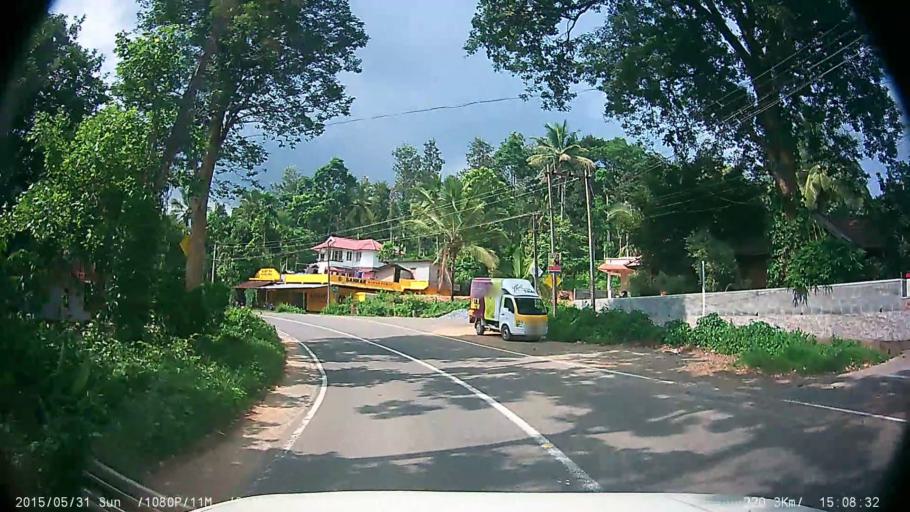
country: IN
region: Kerala
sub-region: Wayanad
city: Kalpetta
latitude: 11.6515
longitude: 76.2169
